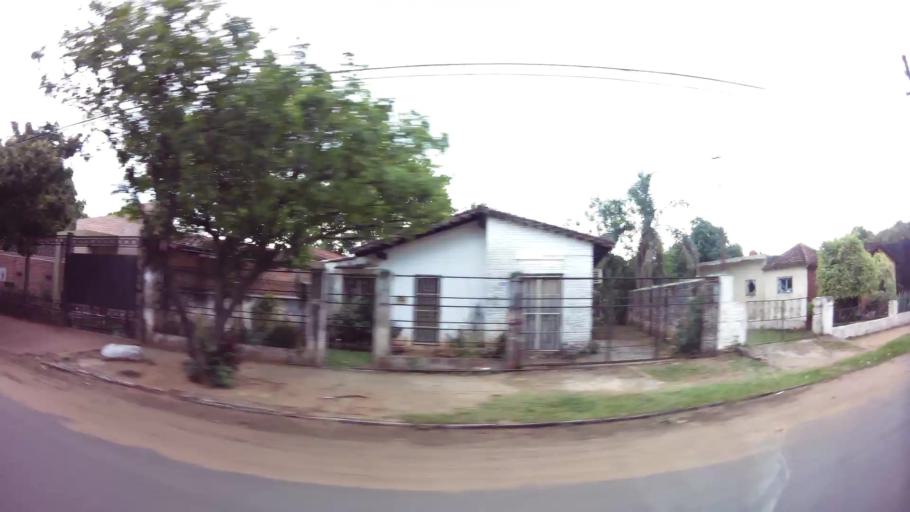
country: PY
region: Central
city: Fernando de la Mora
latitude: -25.3325
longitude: -57.5563
